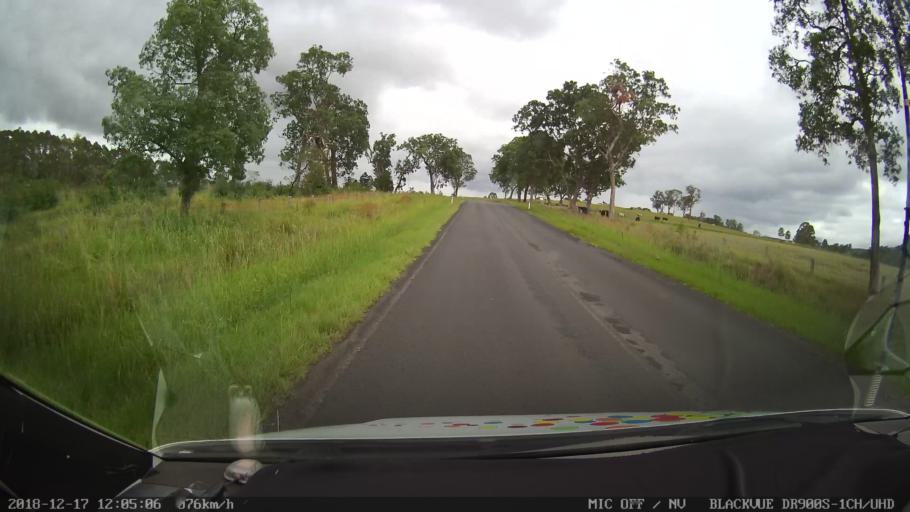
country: AU
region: New South Wales
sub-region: Kyogle
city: Kyogle
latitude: -28.4957
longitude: 152.5675
